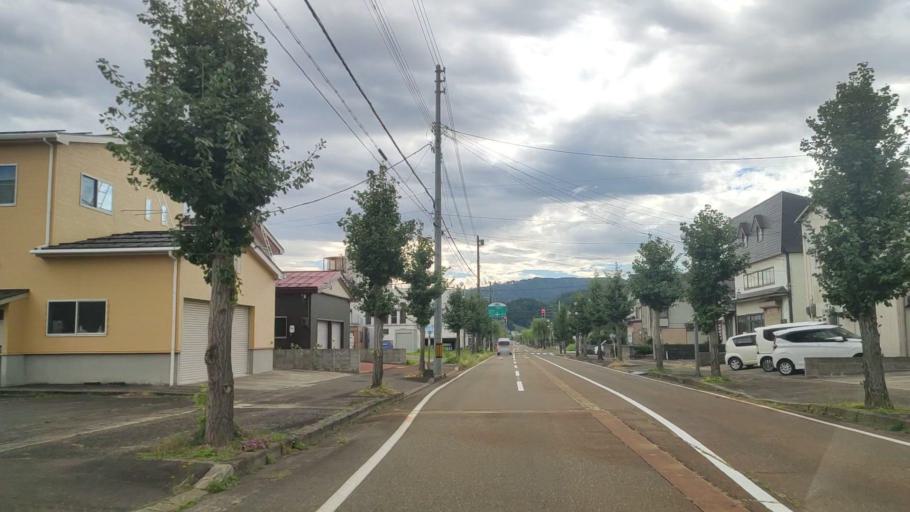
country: JP
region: Niigata
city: Arai
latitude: 37.0204
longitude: 138.2470
